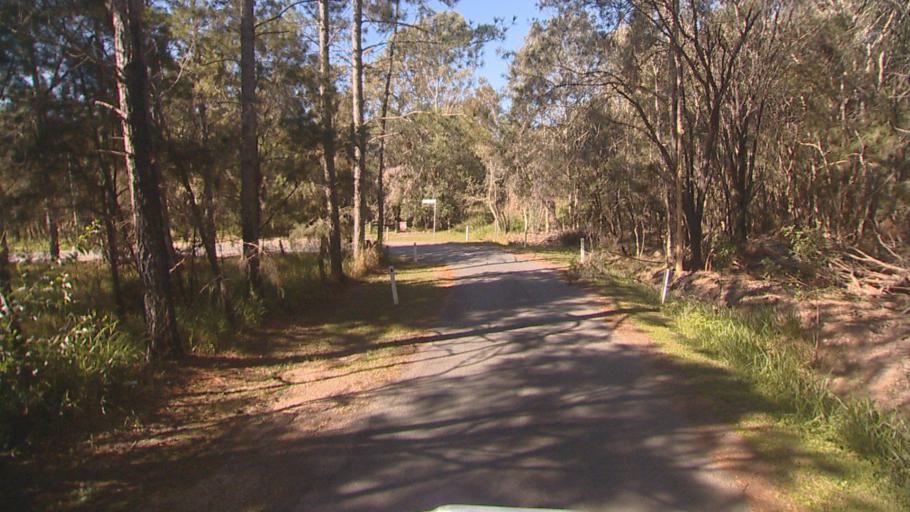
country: AU
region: Queensland
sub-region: Logan
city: Logan Reserve
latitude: -27.7158
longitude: 153.0764
